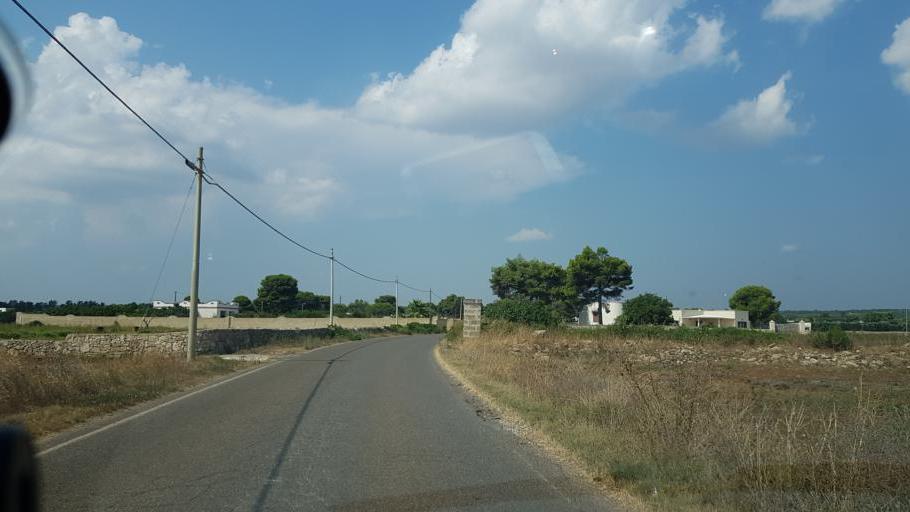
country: IT
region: Apulia
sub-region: Provincia di Taranto
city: Maruggio
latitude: 40.3105
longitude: 17.6322
